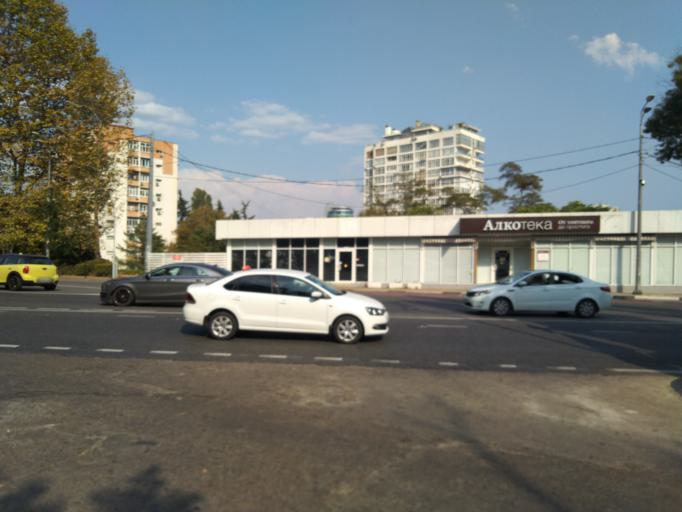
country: RU
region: Krasnodarskiy
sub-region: Sochi City
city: Sochi
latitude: 43.5938
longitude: 39.7174
